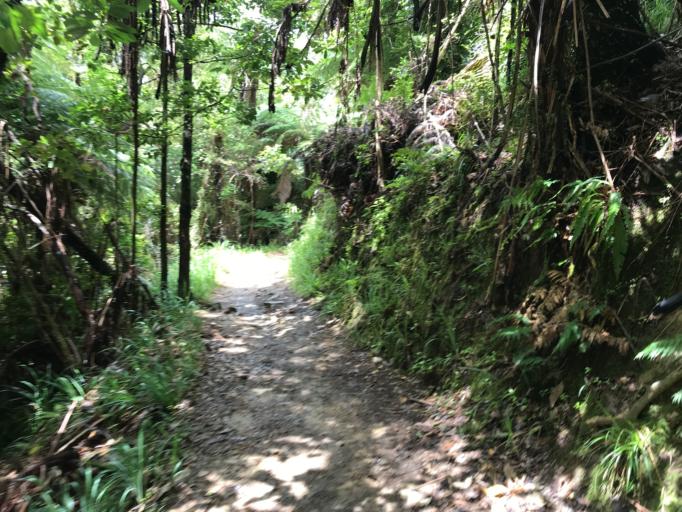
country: NZ
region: Marlborough
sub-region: Marlborough District
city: Picton
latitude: -41.2483
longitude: 173.9543
